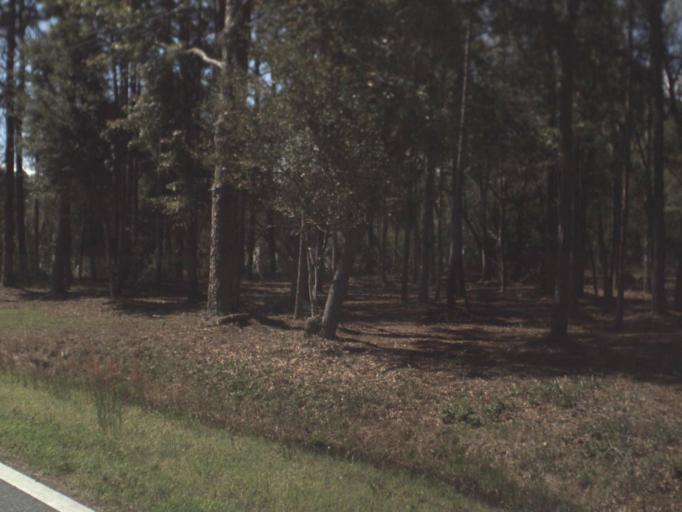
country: US
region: Florida
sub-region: Franklin County
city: Carrabelle
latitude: 29.8890
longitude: -84.5774
